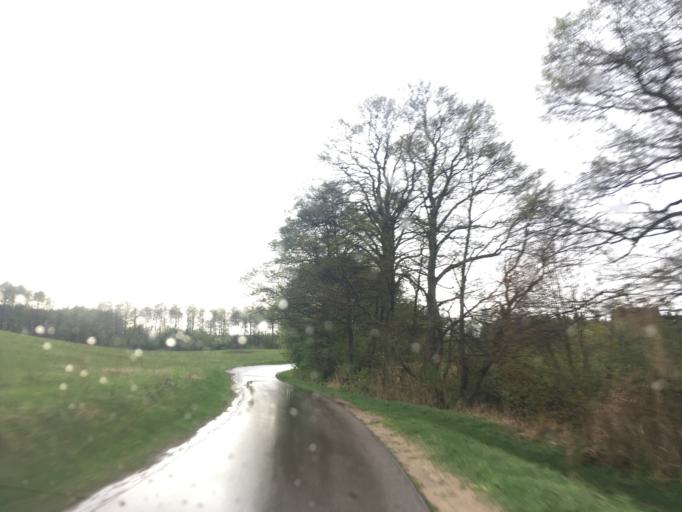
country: PL
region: Warmian-Masurian Voivodeship
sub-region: Powiat dzialdowski
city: Rybno
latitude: 53.3818
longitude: 19.9896
